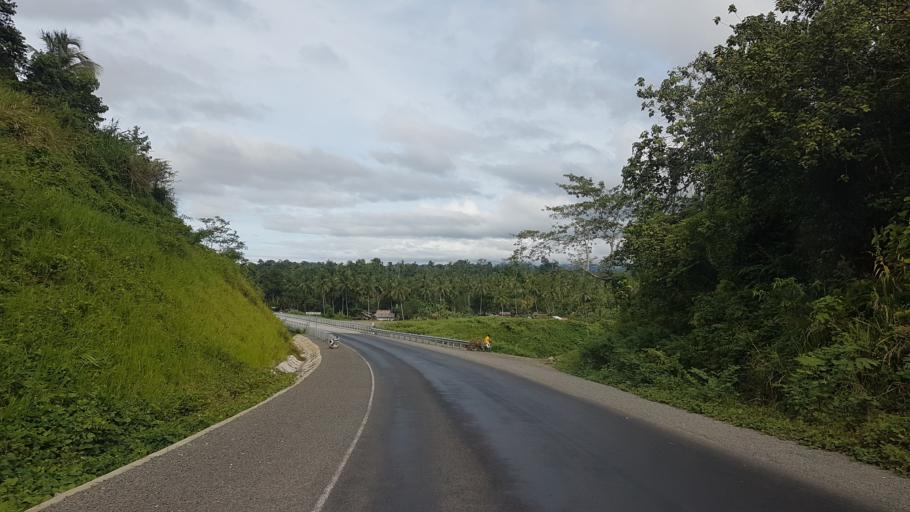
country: PG
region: Northern Province
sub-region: Sohe
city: Popondetta
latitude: -8.8361
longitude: 148.2692
